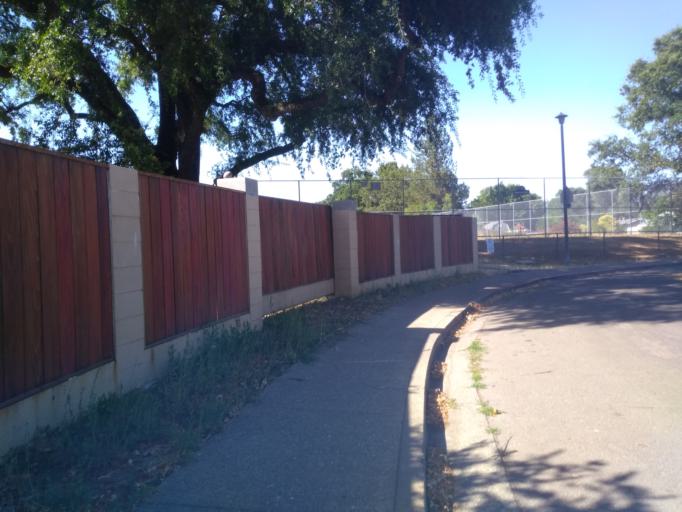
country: US
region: California
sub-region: Mendocino County
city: Ukiah
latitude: 39.1317
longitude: -123.2118
